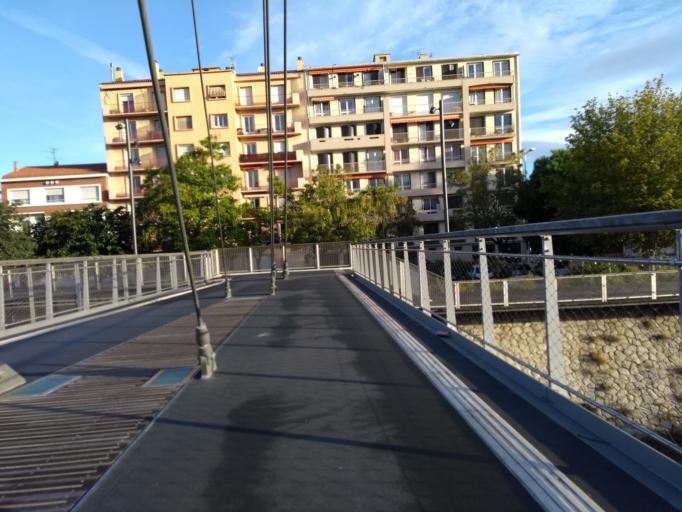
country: FR
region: Languedoc-Roussillon
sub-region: Departement des Pyrenees-Orientales
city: Perpignan
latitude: 42.7030
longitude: 2.8884
